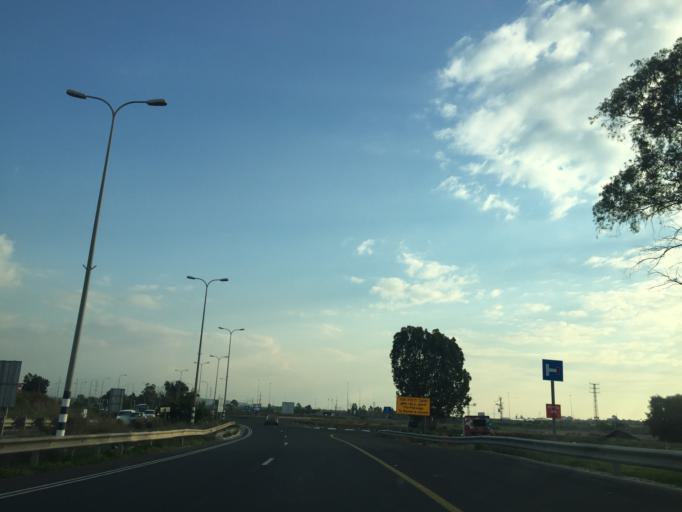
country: IL
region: Central District
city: Ramla
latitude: 31.9194
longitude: 34.8855
